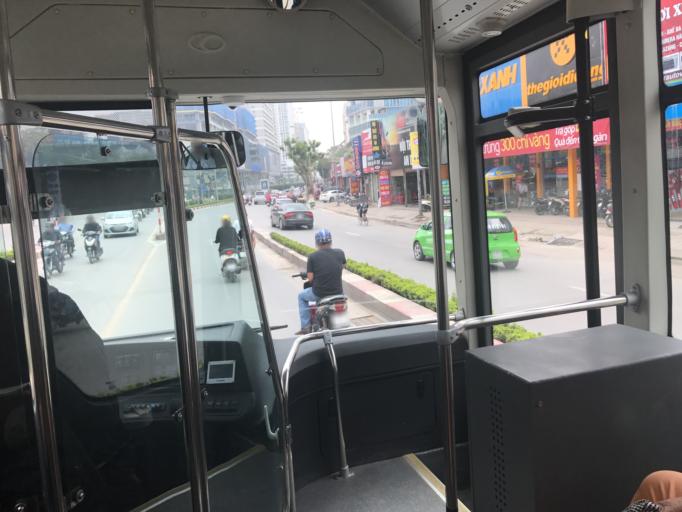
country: VN
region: Ha Noi
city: Thanh Xuan
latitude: 21.0091
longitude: 105.8096
